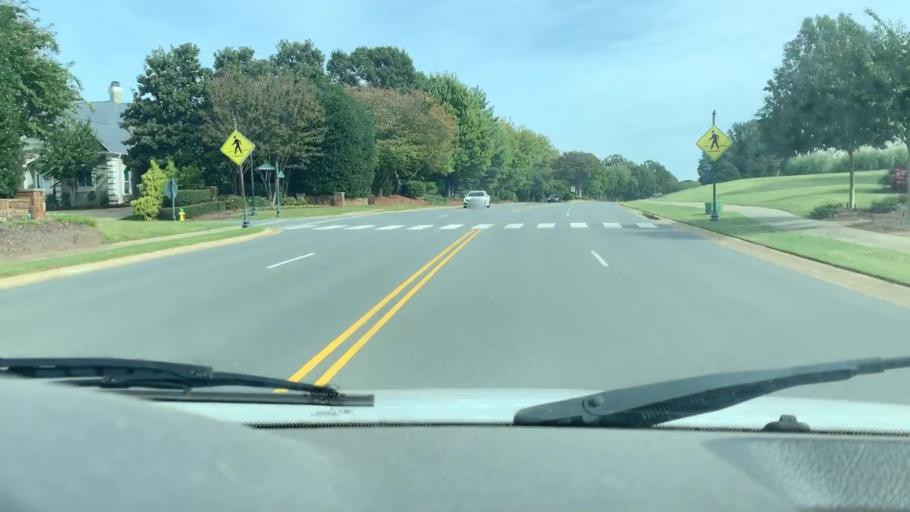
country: US
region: North Carolina
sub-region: Mecklenburg County
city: Cornelius
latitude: 35.4720
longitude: -80.9188
